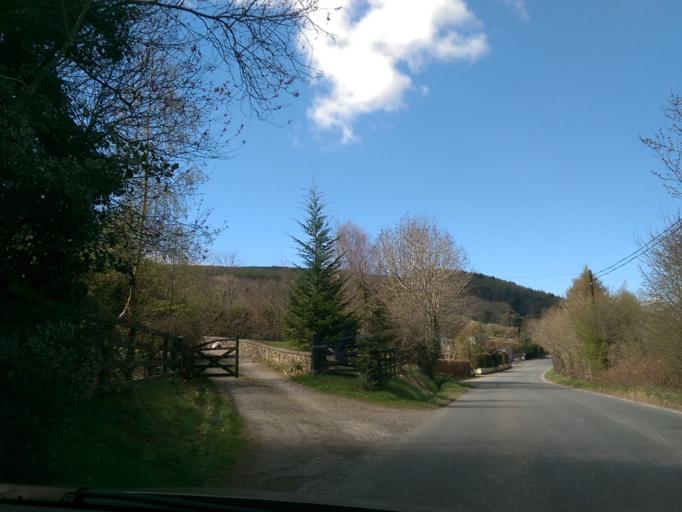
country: IE
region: Leinster
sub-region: Wicklow
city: Carnew
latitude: 52.8057
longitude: -6.4797
